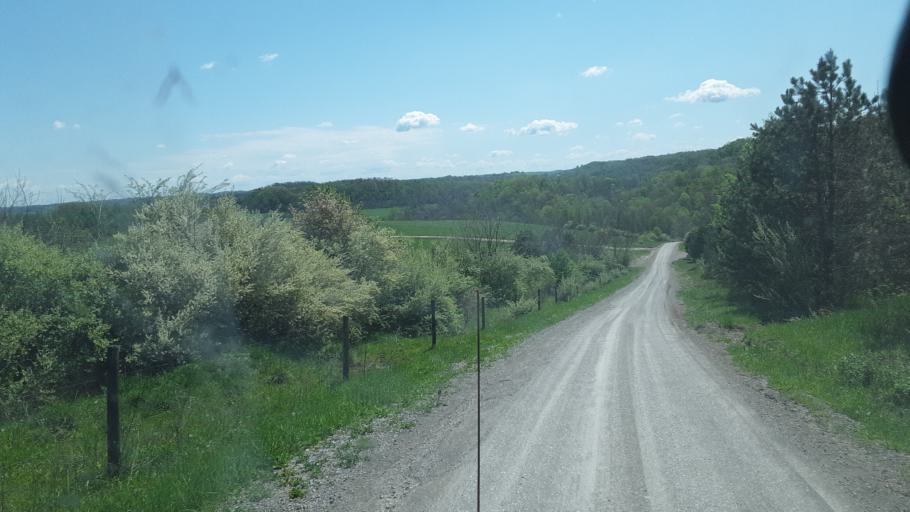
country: US
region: Ohio
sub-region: Noble County
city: Caldwell
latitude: 39.7715
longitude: -81.6088
